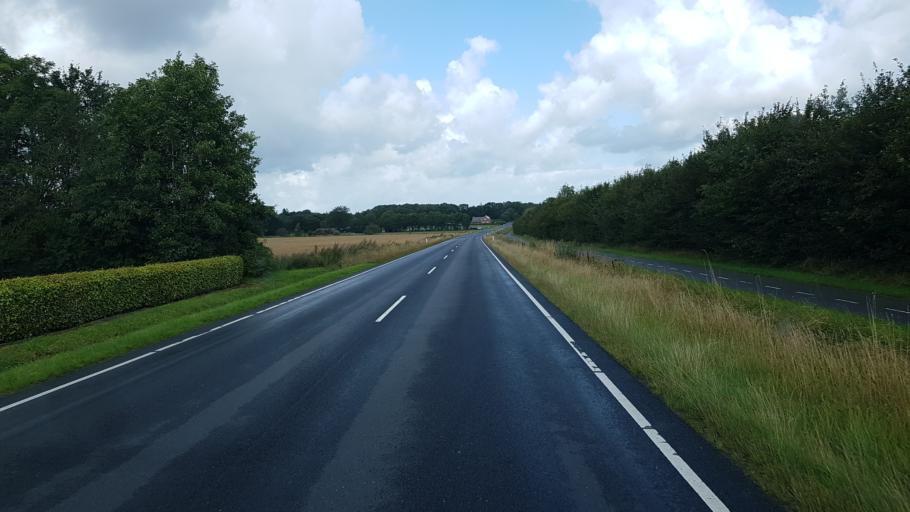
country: DK
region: South Denmark
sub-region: Vejen Kommune
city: Vejen
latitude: 55.5278
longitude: 9.1142
